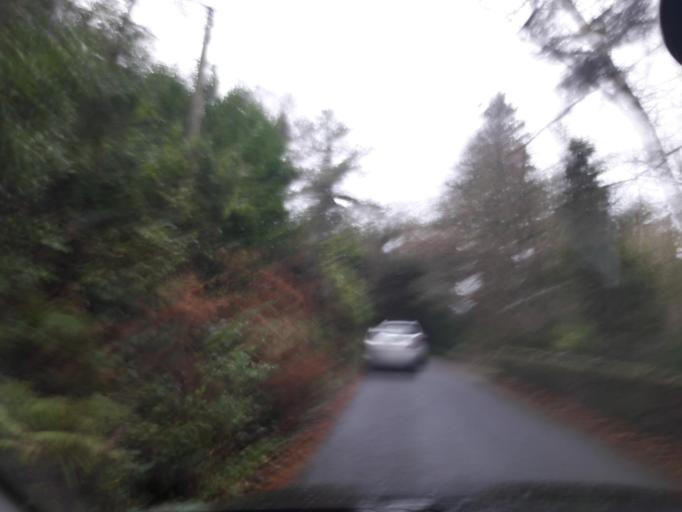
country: IE
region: Ulster
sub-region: County Donegal
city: Buncrana
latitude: 55.2195
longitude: -7.6117
